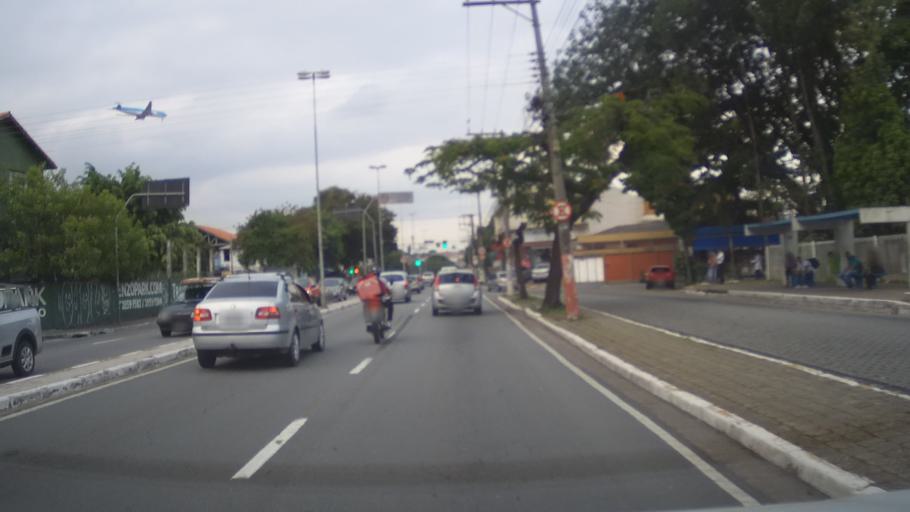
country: BR
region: Sao Paulo
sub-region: Guarulhos
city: Guarulhos
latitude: -23.4522
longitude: -46.5166
